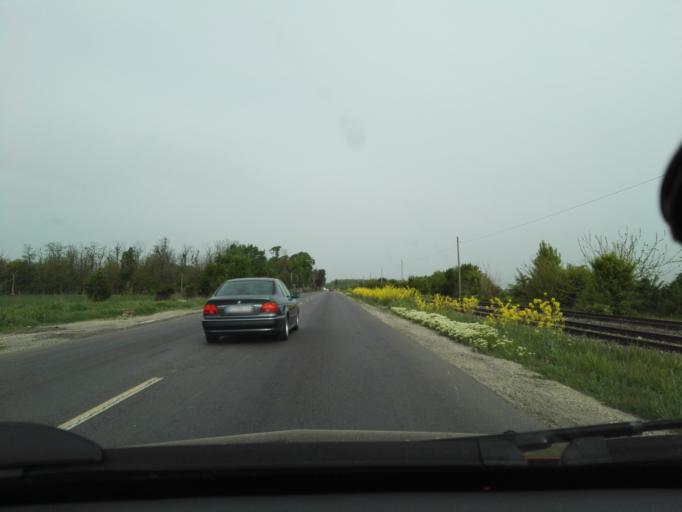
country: RO
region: Ilfov
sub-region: Comuna Jilava
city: Jilava
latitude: 44.3472
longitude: 26.0733
